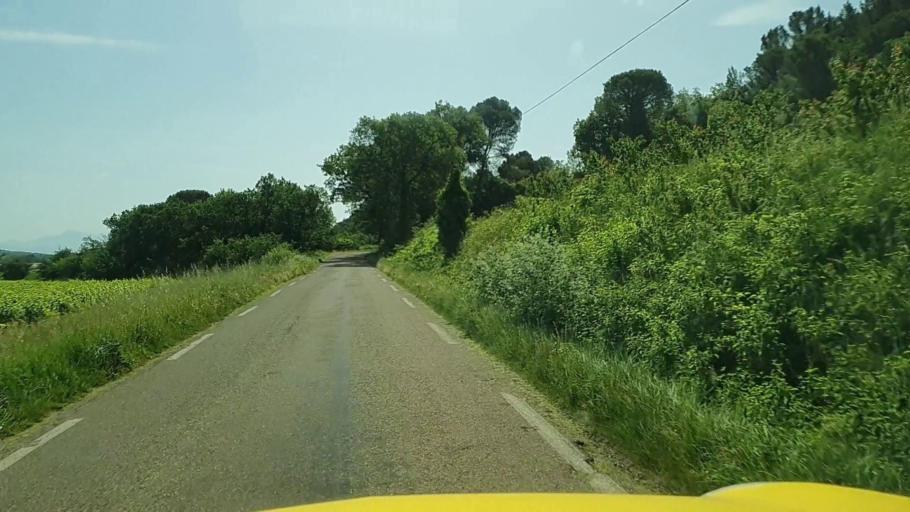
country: FR
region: Languedoc-Roussillon
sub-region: Departement du Gard
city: Connaux
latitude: 44.0917
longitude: 4.5790
